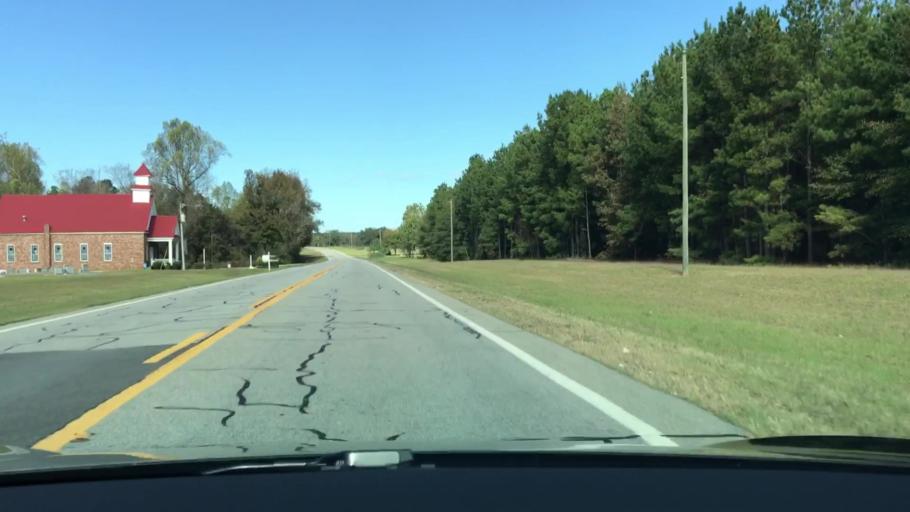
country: US
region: Georgia
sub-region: Glascock County
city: Gibson
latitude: 33.3384
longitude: -82.5718
